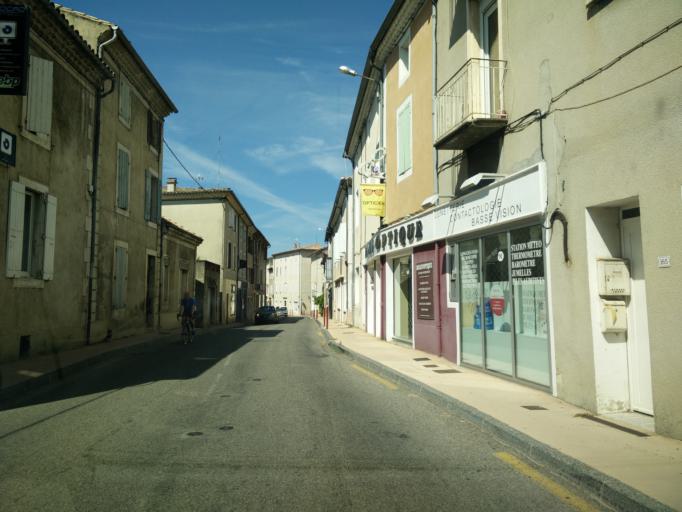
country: FR
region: Rhone-Alpes
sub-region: Departement de la Drome
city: La Begude-de-Mazenc
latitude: 44.5445
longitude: 4.9372
